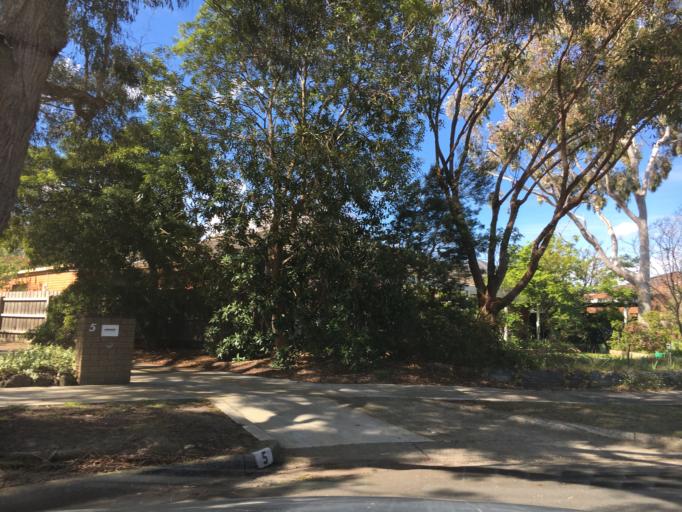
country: AU
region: Victoria
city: Clayton
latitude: -37.8969
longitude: 145.1203
